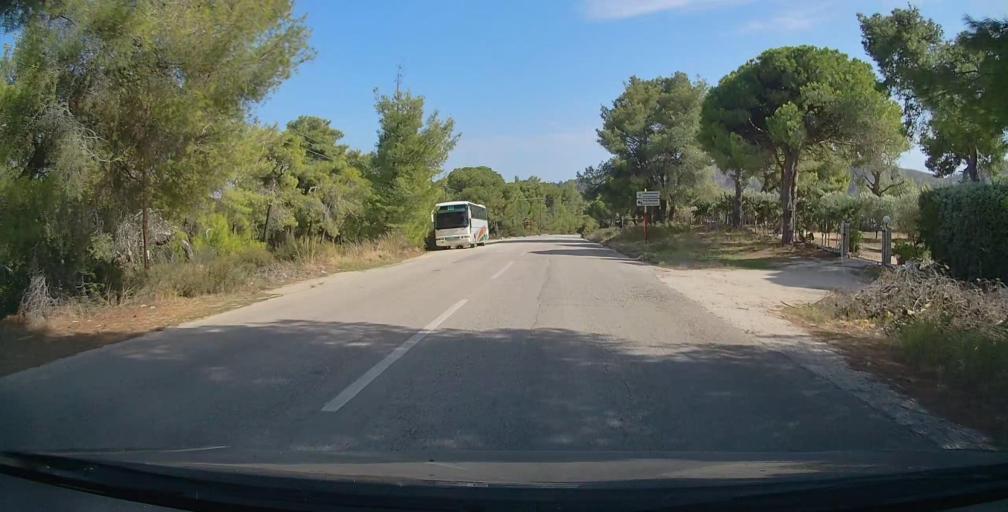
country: GR
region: Central Macedonia
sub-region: Nomos Chalkidikis
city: Sarti
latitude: 40.1240
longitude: 23.9667
